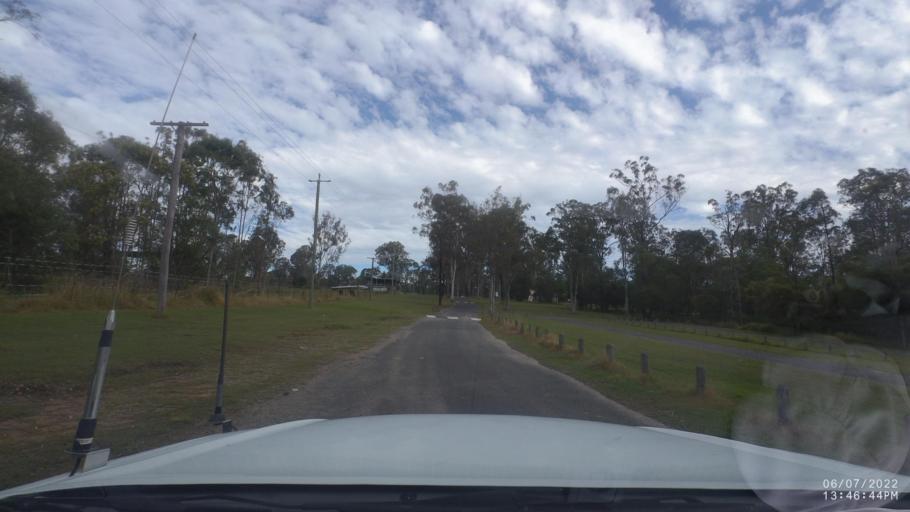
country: AU
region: Queensland
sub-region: Logan
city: Cedar Vale
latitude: -27.8467
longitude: 153.0298
